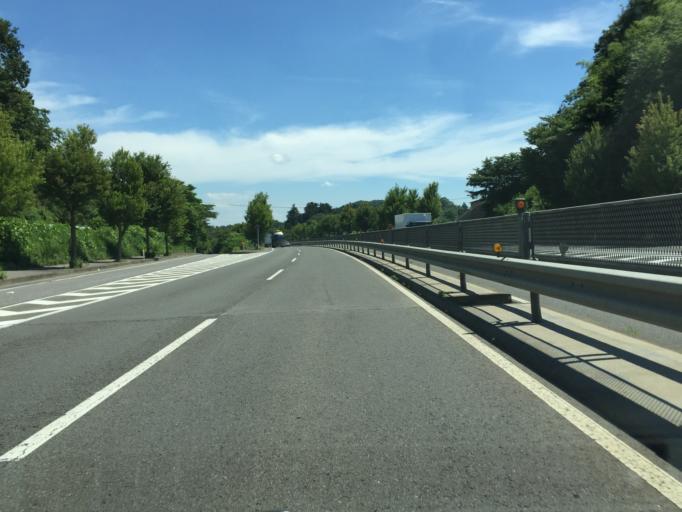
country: JP
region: Fukushima
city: Fukushima-shi
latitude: 37.6738
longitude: 140.4794
